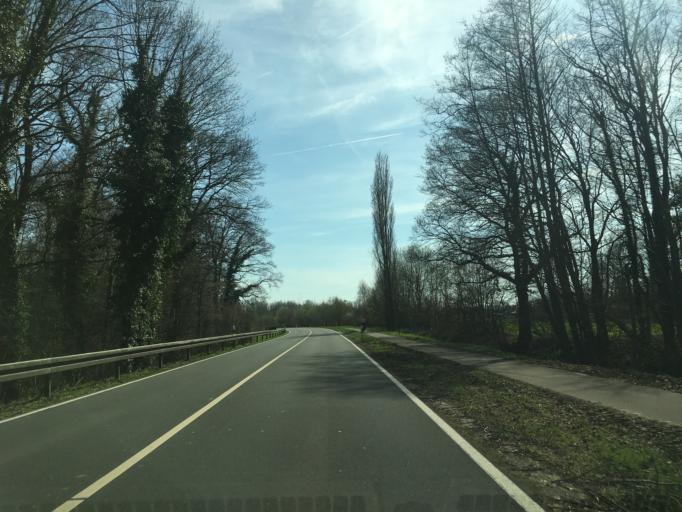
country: DE
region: North Rhine-Westphalia
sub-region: Regierungsbezirk Munster
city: Greven
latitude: 52.0552
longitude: 7.6138
